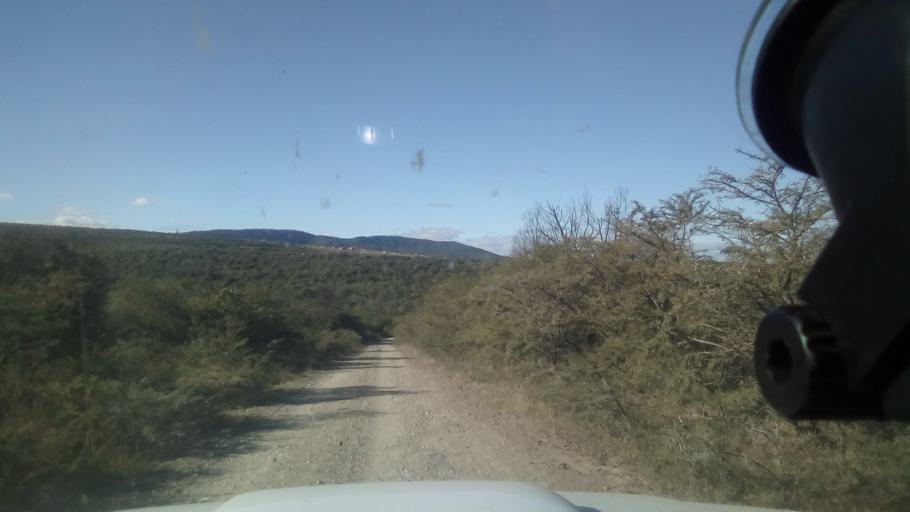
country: ZA
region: Eastern Cape
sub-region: Buffalo City Metropolitan Municipality
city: Bhisho
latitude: -32.7538
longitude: 27.3378
